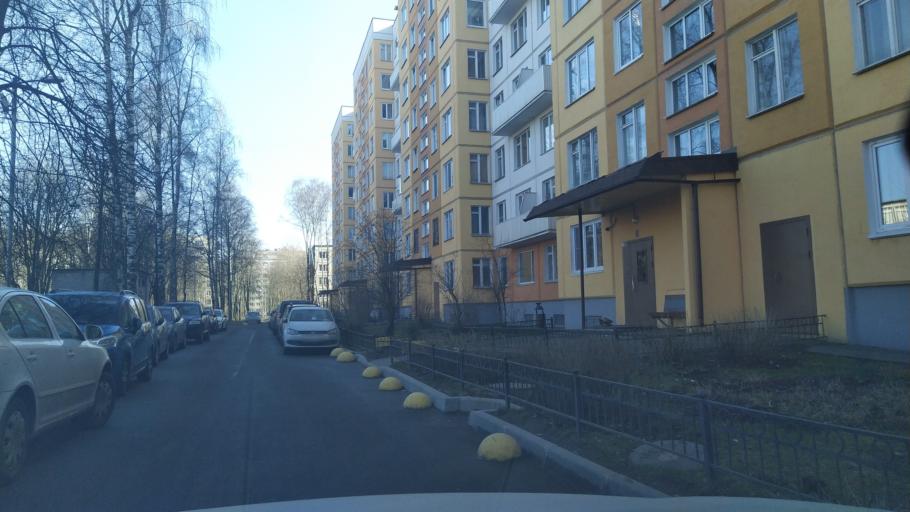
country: RU
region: Leningrad
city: Akademicheskoe
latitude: 60.0203
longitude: 30.3959
